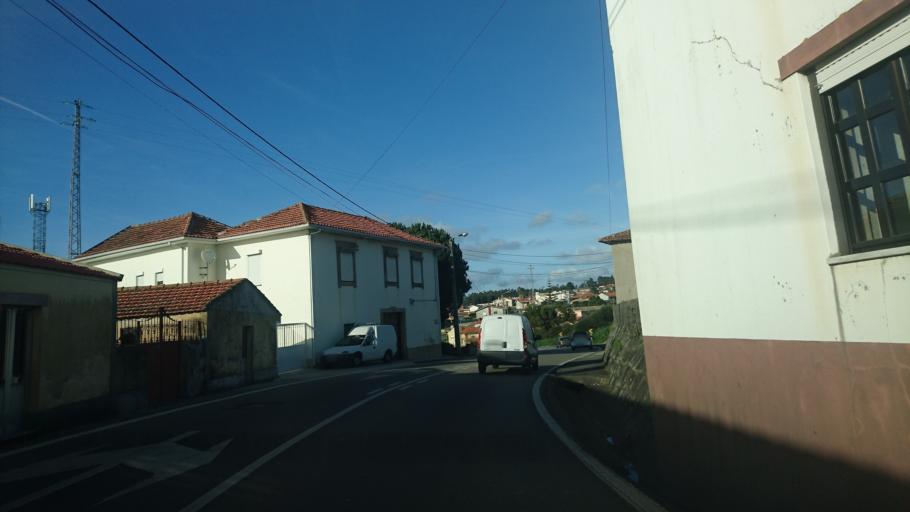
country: PT
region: Aveiro
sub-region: Espinho
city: Souto
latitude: 40.9753
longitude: -8.6305
